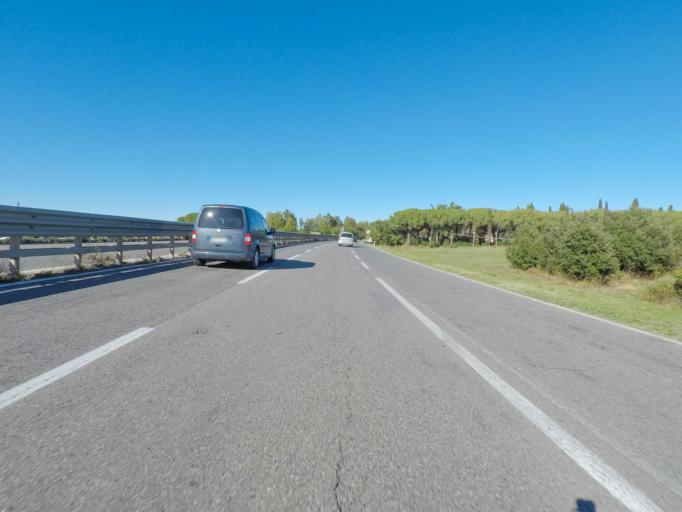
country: IT
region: Tuscany
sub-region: Provincia di Grosseto
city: Grosseto
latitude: 42.7026
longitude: 11.1374
